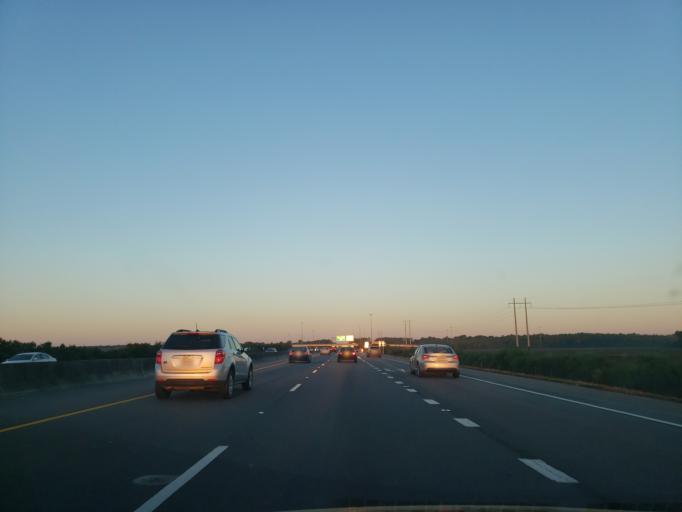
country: US
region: Georgia
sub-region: Chatham County
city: Georgetown
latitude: 31.9844
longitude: -81.1909
